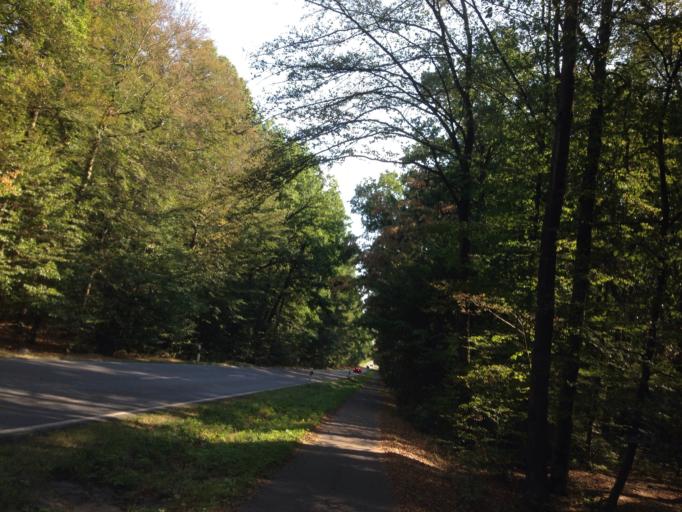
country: DE
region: Hesse
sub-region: Regierungsbezirk Giessen
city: Giessen
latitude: 50.5510
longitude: 8.7006
